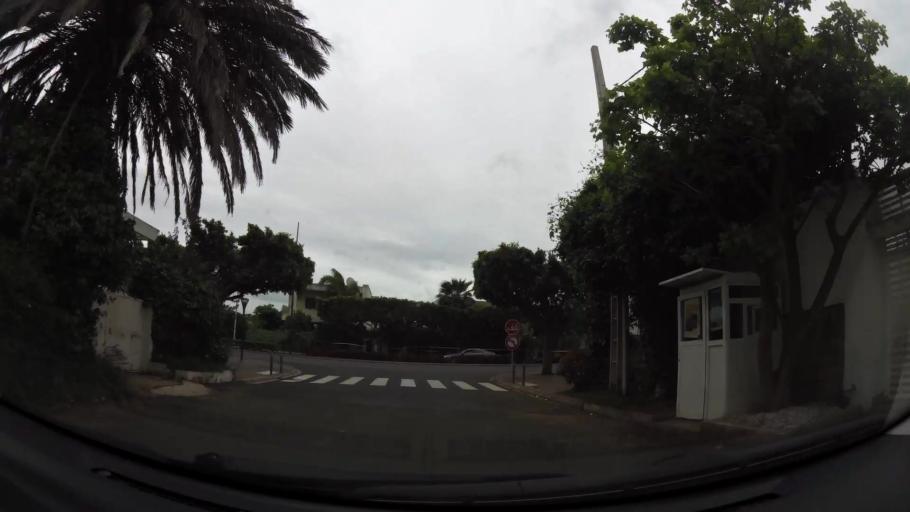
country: MA
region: Grand Casablanca
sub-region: Casablanca
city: Casablanca
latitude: 33.5858
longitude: -7.6537
